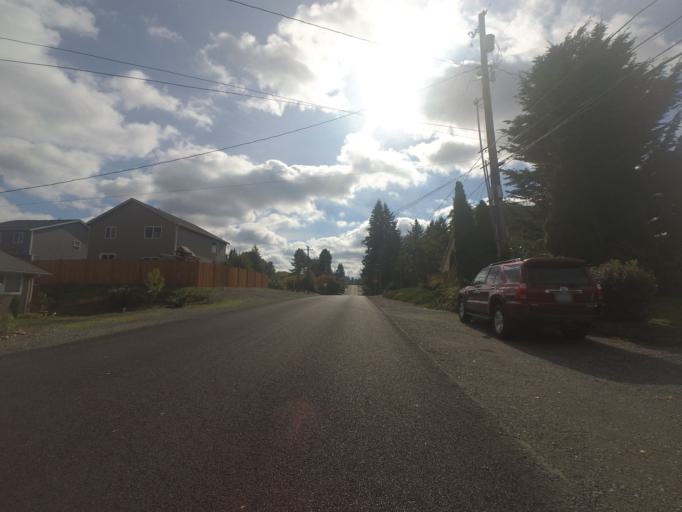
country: US
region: Washington
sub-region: Pierce County
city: University Place
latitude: 47.2322
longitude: -122.5440
